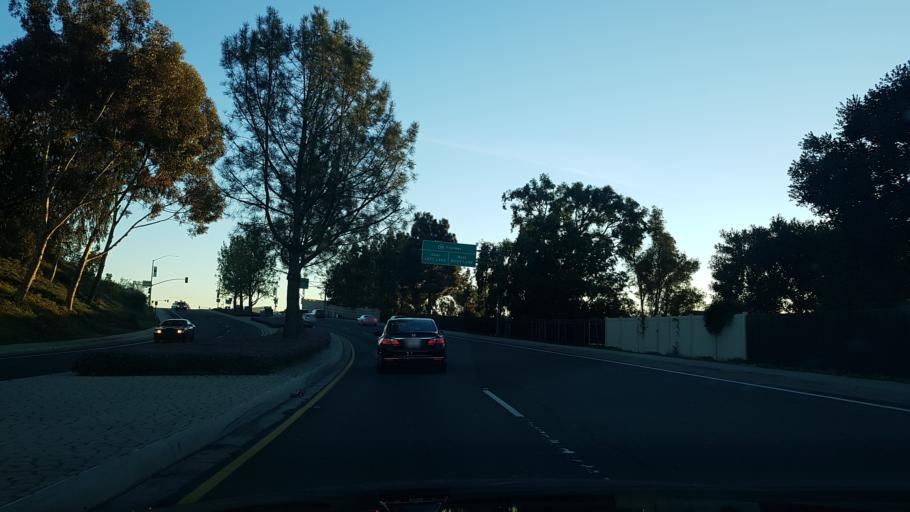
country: US
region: California
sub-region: San Diego County
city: Fairbanks Ranch
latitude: 32.9564
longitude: -117.1296
